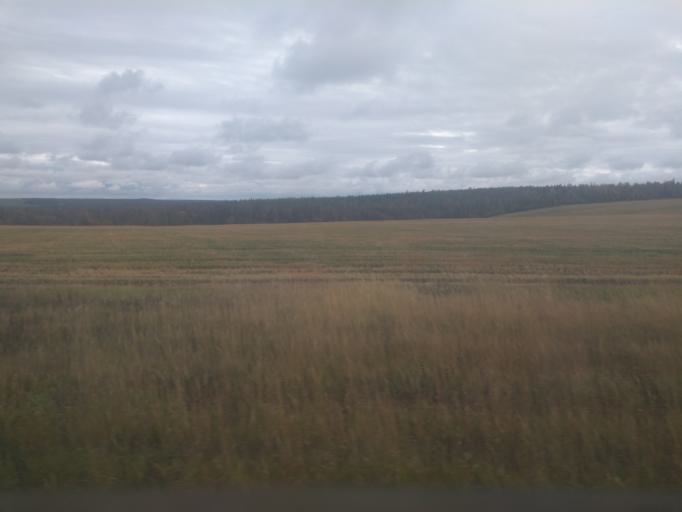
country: RU
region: Udmurtiya
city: Alnashi
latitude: 56.1399
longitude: 52.5686
